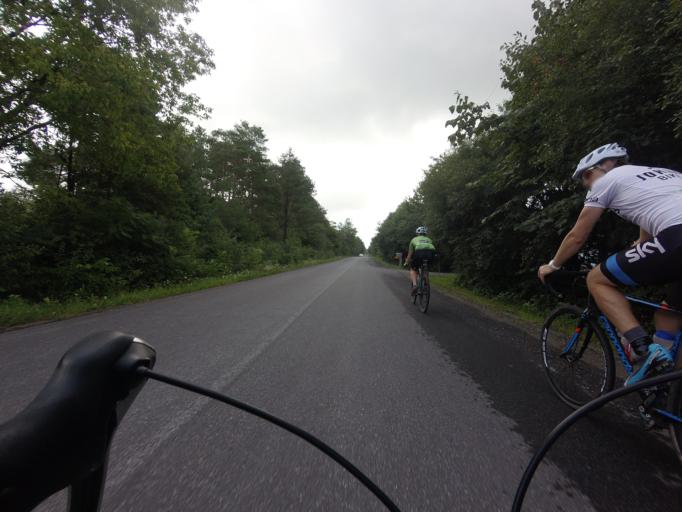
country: CA
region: Ontario
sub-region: Lanark County
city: Smiths Falls
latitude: 44.9537
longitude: -75.7938
